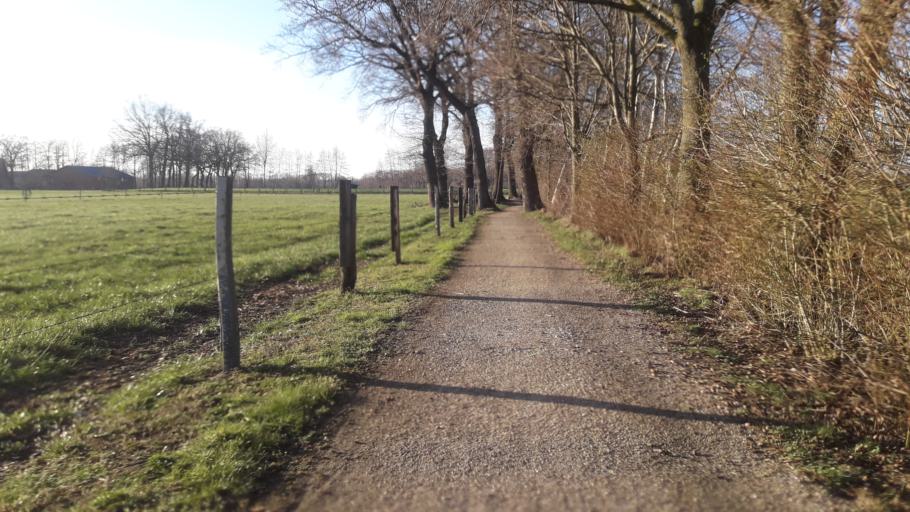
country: DE
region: North Rhine-Westphalia
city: Rietberg
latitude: 51.7823
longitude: 8.4805
